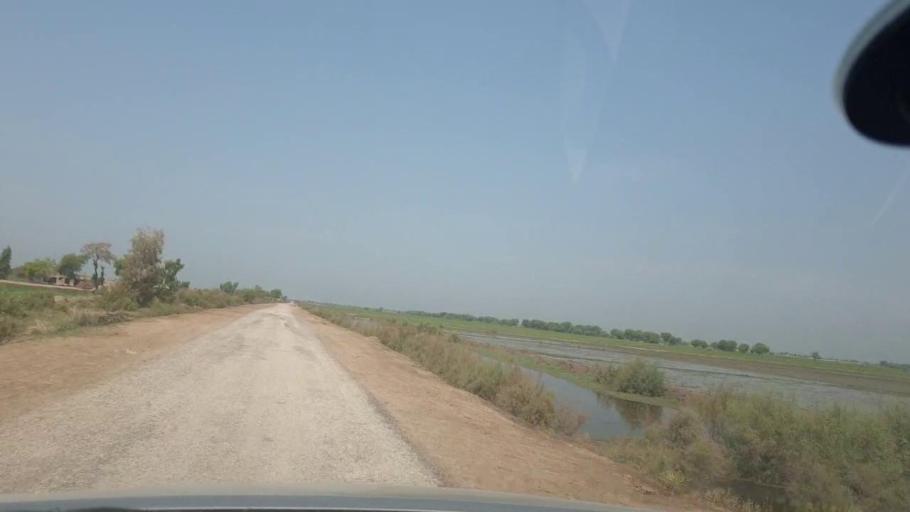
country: PK
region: Balochistan
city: Mehrabpur
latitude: 28.0643
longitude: 68.0632
